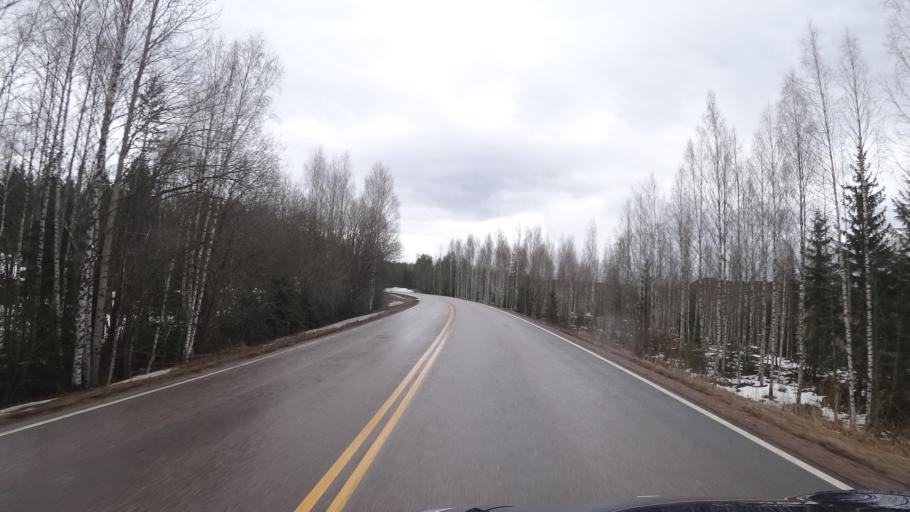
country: FI
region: Uusimaa
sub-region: Loviisa
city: Lapinjaervi
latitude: 60.7351
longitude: 26.1873
